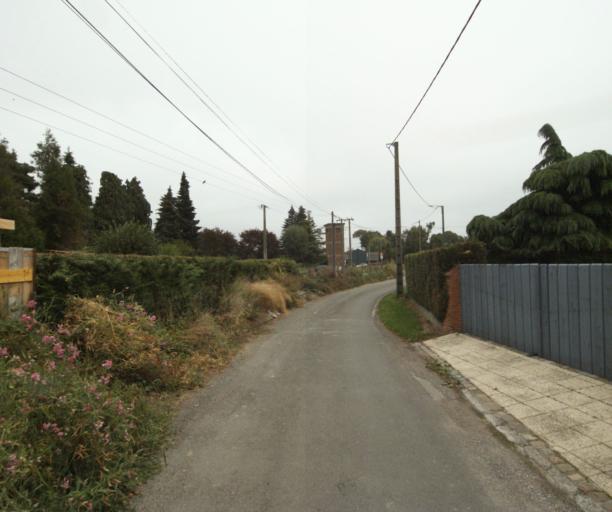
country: FR
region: Nord-Pas-de-Calais
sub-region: Departement du Nord
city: Baisieux
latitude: 50.6211
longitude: 3.2471
